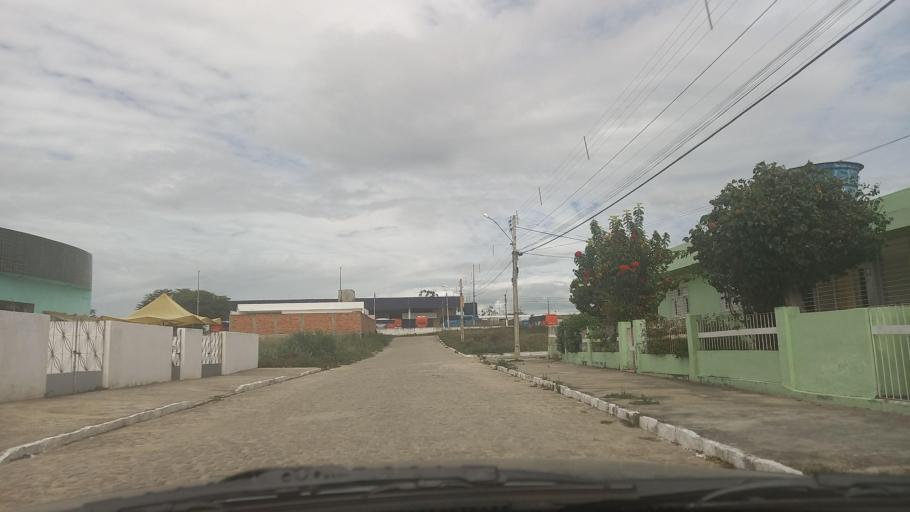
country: BR
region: Pernambuco
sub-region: Caruaru
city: Caruaru
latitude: -8.2934
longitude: -35.9899
